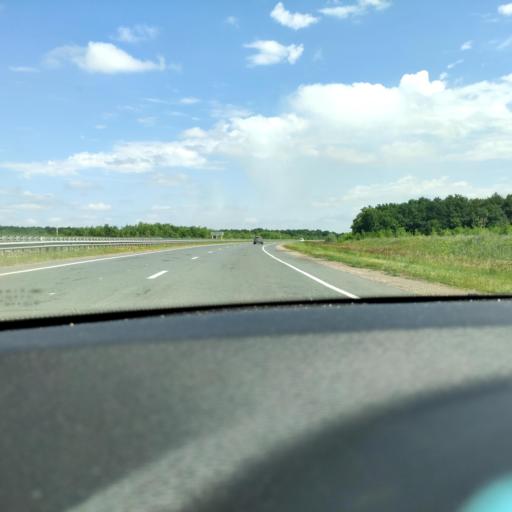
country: RU
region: Samara
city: Petra-Dubrava
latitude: 53.3371
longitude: 50.4323
